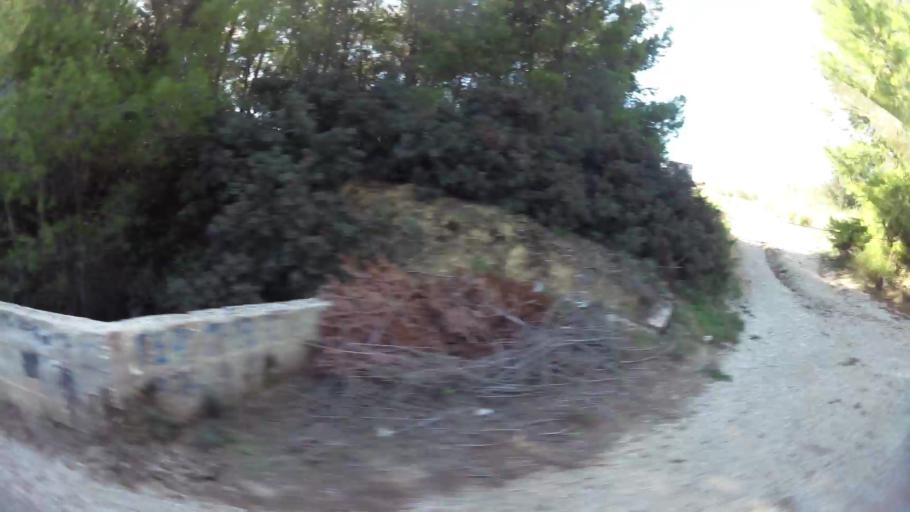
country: GR
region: Attica
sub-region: Nomarchia Anatolikis Attikis
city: Dioni
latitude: 38.0164
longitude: 23.9287
